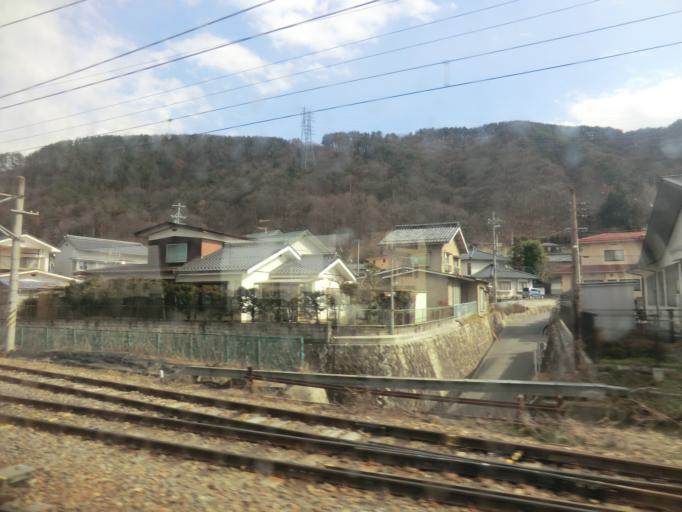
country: JP
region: Nagano
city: Hotaka
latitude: 36.3522
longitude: 137.9281
